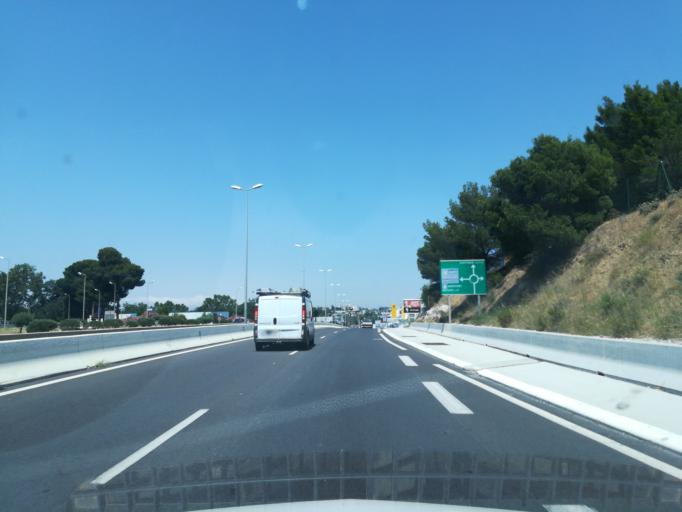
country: FR
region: Languedoc-Roussillon
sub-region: Departement des Pyrenees-Orientales
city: Perpignan
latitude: 42.6706
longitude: 2.8855
